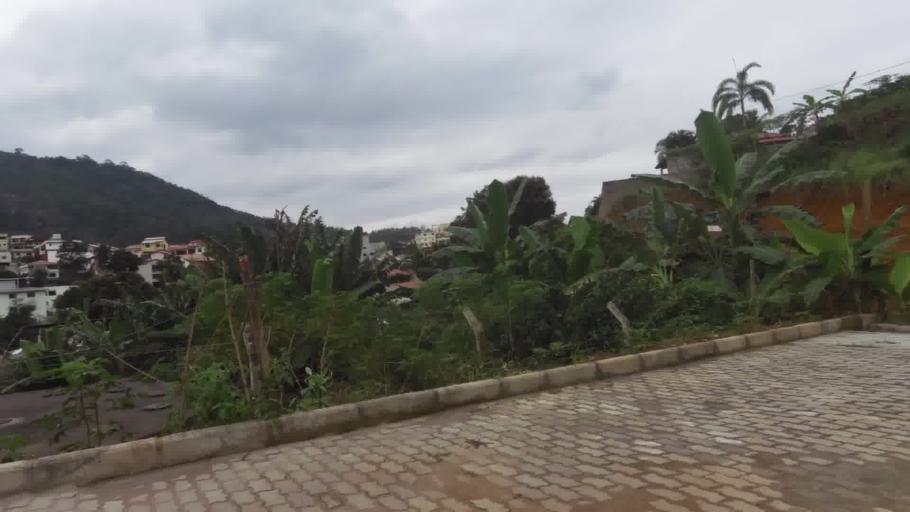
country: BR
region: Espirito Santo
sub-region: Iconha
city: Iconha
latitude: -20.7912
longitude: -40.8153
